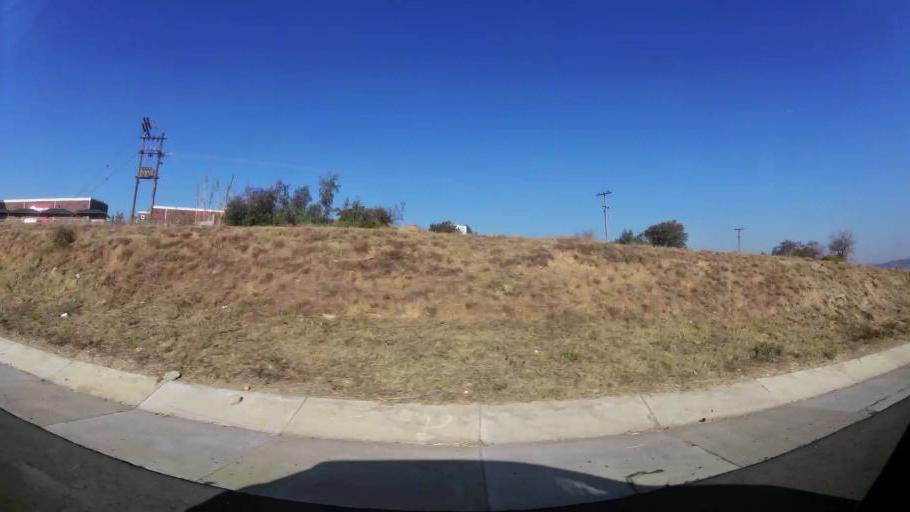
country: ZA
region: Gauteng
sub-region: West Rand District Municipality
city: Muldersdriseloop
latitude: -26.0251
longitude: 27.8519
